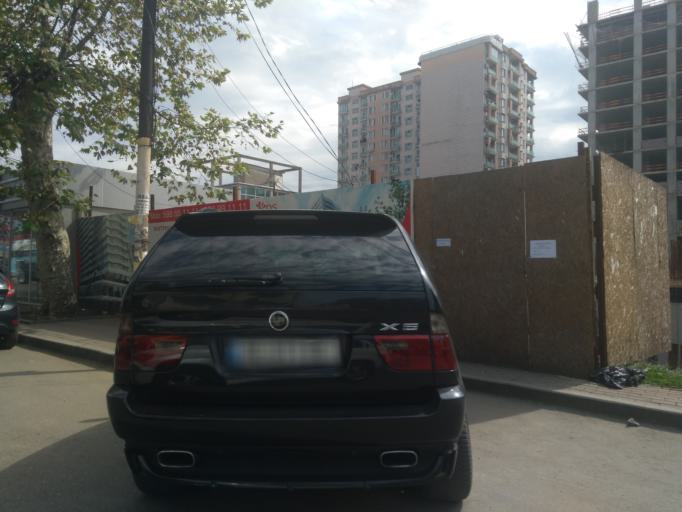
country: GE
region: Ajaria
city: Batumi
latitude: 41.6411
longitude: 41.6317
